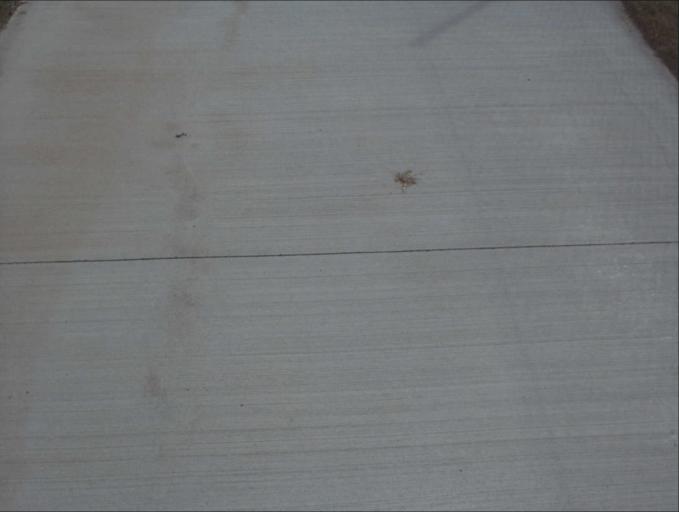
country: AU
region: Queensland
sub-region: Logan
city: Logan Reserve
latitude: -27.6891
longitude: 153.0696
